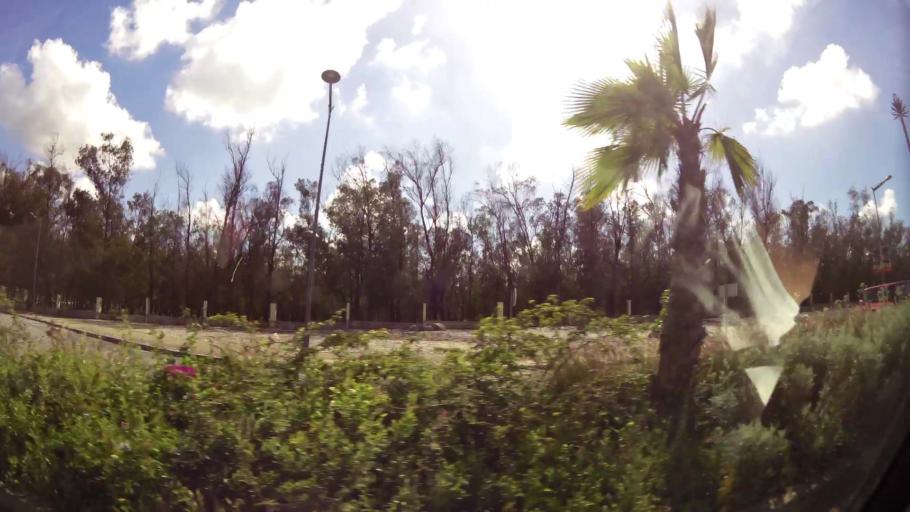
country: MA
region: Grand Casablanca
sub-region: Nouaceur
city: Bouskoura
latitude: 33.4761
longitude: -7.6198
